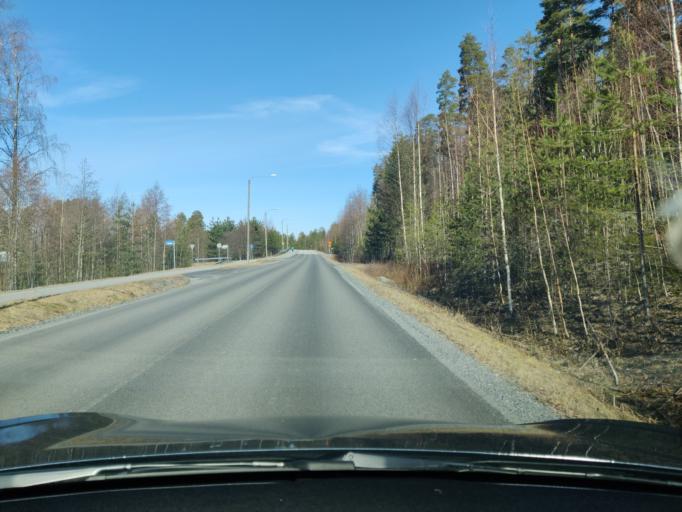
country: FI
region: Northern Savo
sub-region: Kuopio
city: Vehmersalmi
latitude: 62.7687
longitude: 28.0106
